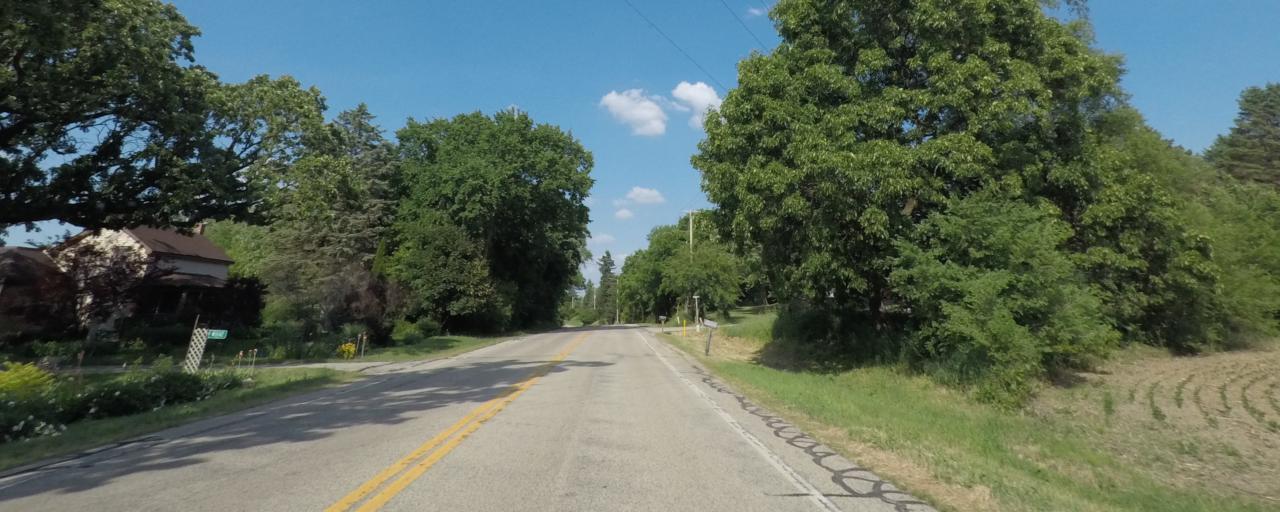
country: US
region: Wisconsin
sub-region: Walworth County
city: Potter Lake
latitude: 42.8064
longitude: -88.3599
